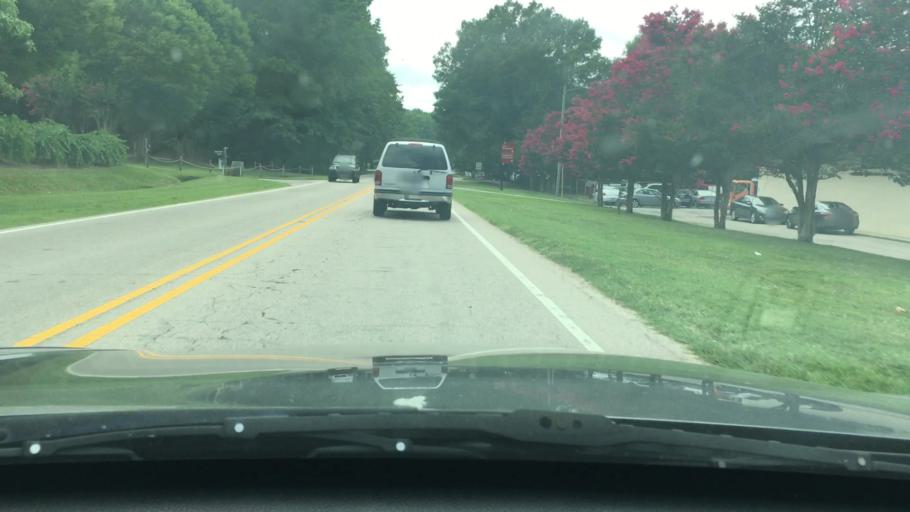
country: US
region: North Carolina
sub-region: Wake County
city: Cary
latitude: 35.7924
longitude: -78.7741
